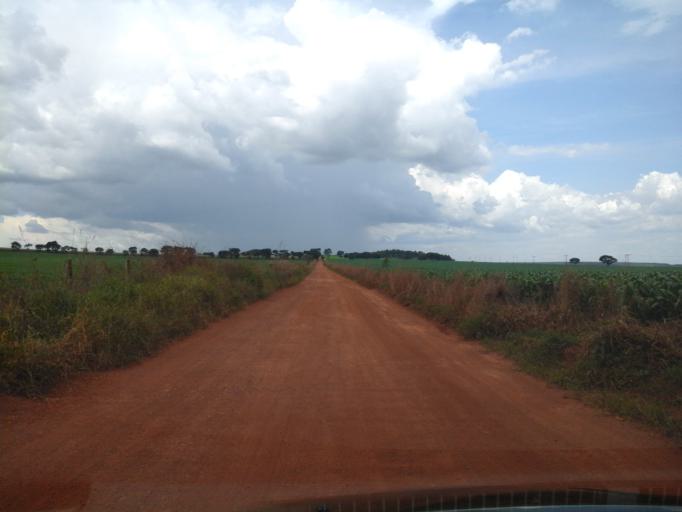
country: BR
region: Goias
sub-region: Abadiania
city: Abadiania
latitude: -15.9953
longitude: -48.5409
